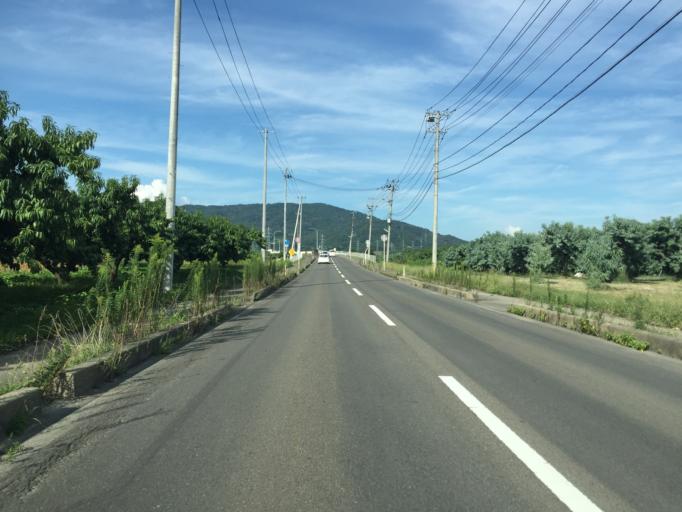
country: JP
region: Fukushima
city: Fukushima-shi
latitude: 37.8158
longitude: 140.4635
